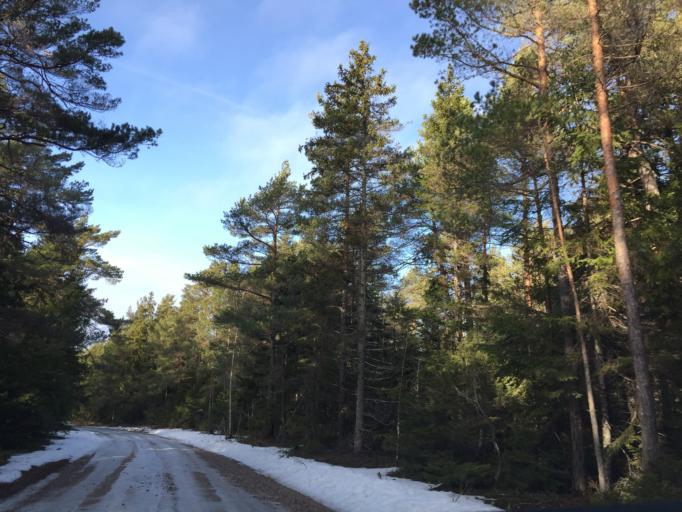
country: EE
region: Saare
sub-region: Kuressaare linn
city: Kuressaare
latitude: 58.4738
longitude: 21.9581
